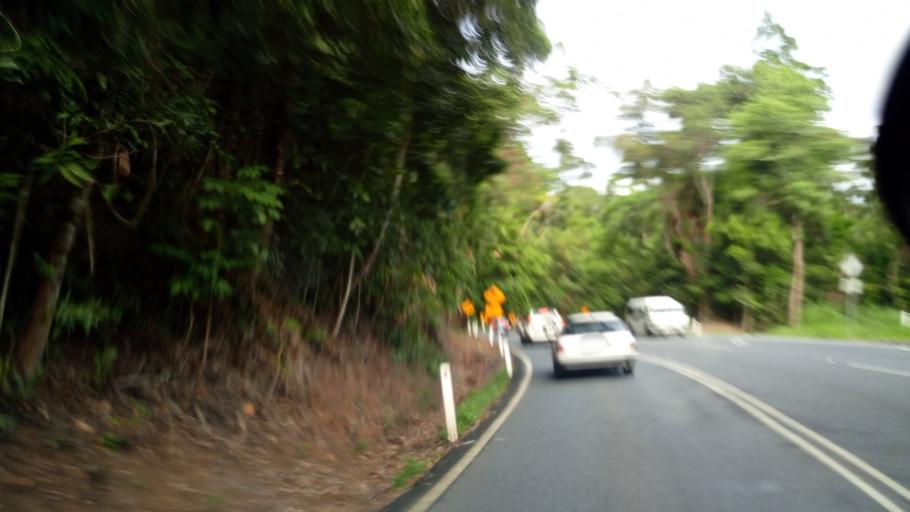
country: AU
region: Queensland
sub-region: Tablelands
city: Kuranda
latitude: -16.8304
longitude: 145.6597
